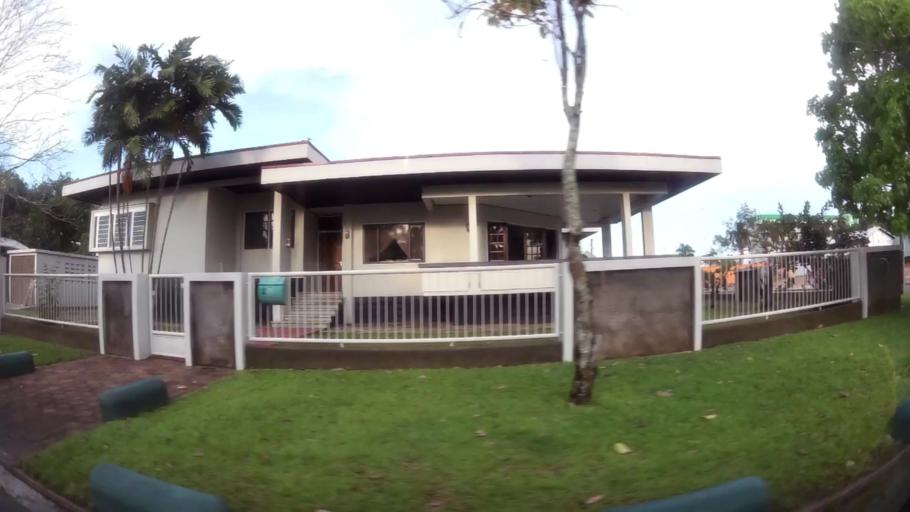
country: SR
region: Paramaribo
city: Paramaribo
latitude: 5.8368
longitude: -55.1857
